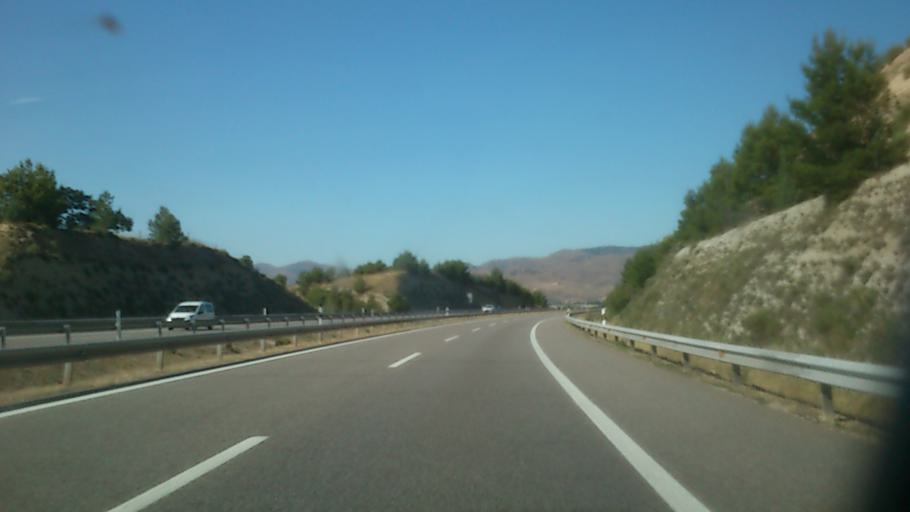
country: ES
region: Aragon
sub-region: Provincia de Zaragoza
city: Calatayud
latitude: 41.3442
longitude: -1.6299
